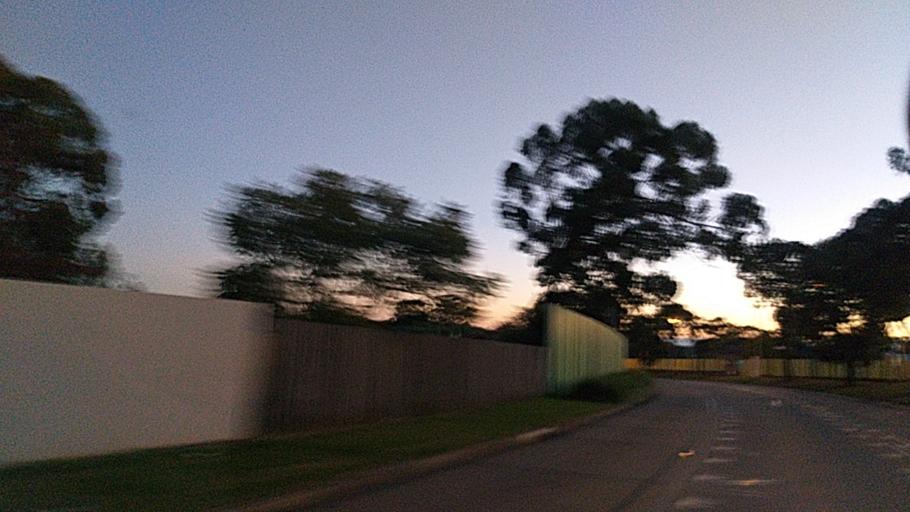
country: AU
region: New South Wales
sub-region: Campbelltown Municipality
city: Campbelltown
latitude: -34.0629
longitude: 150.8249
